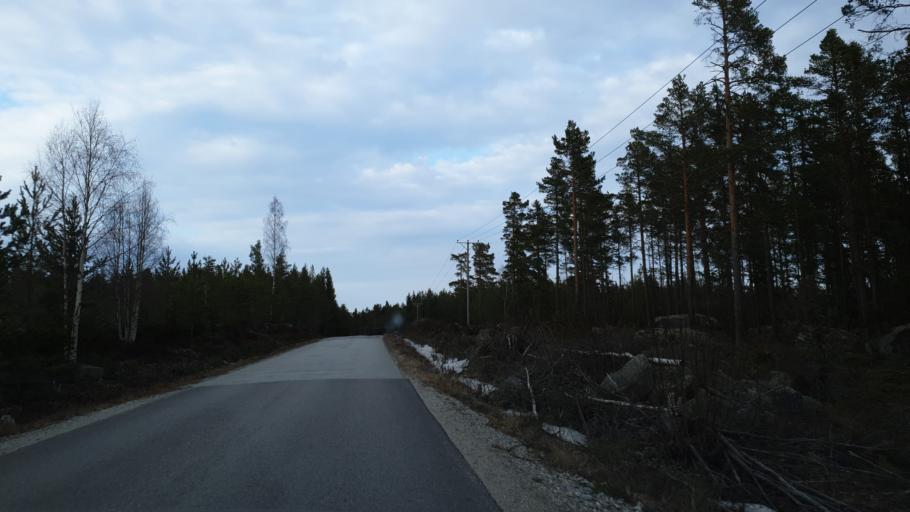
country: SE
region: Vaesternorrland
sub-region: Sundsvalls Kommun
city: Njurundabommen
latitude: 61.9950
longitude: 17.3846
